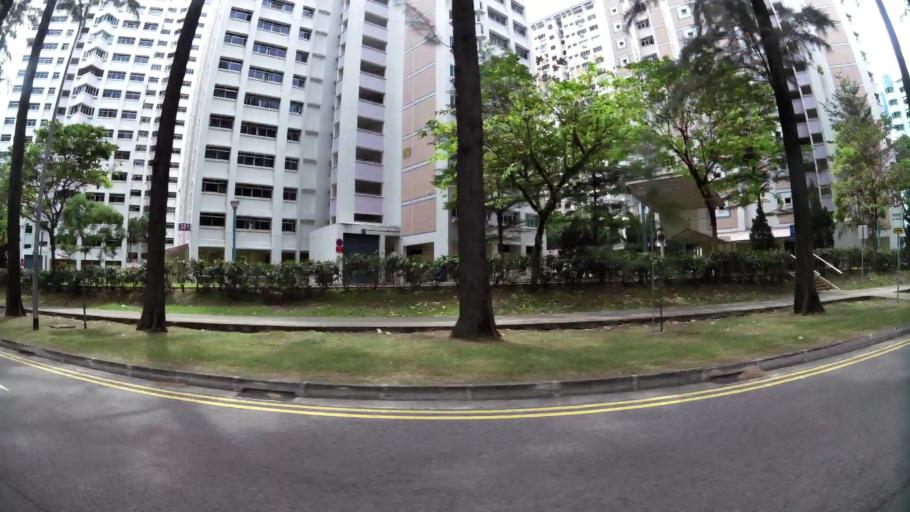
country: MY
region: Johor
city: Johor Bahru
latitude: 1.3377
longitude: 103.7247
